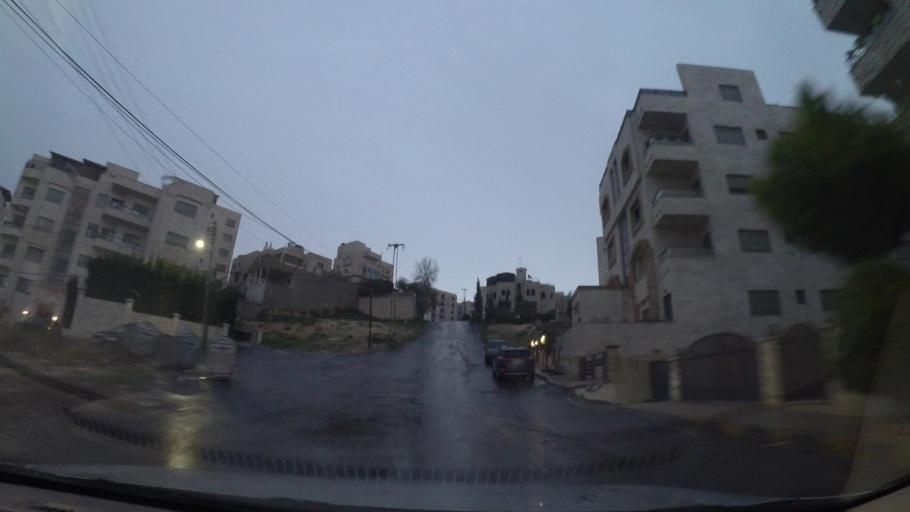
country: JO
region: Amman
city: Umm as Summaq
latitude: 31.9015
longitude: 35.8636
